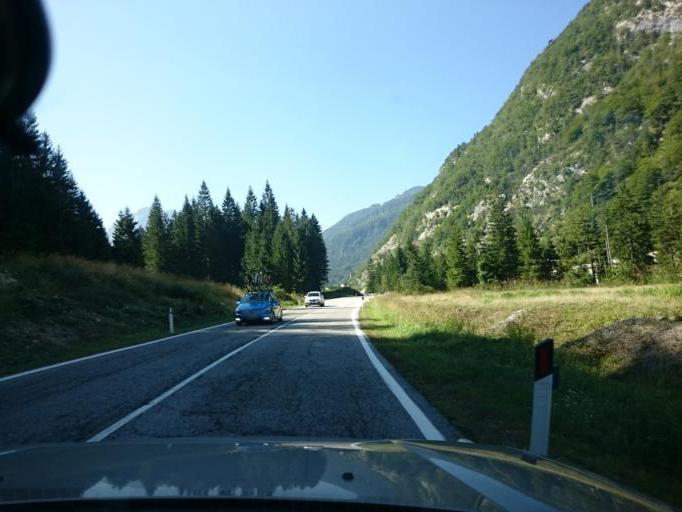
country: IT
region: Friuli Venezia Giulia
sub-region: Provincia di Udine
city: Tarvisio
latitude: 46.4498
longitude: 13.5748
